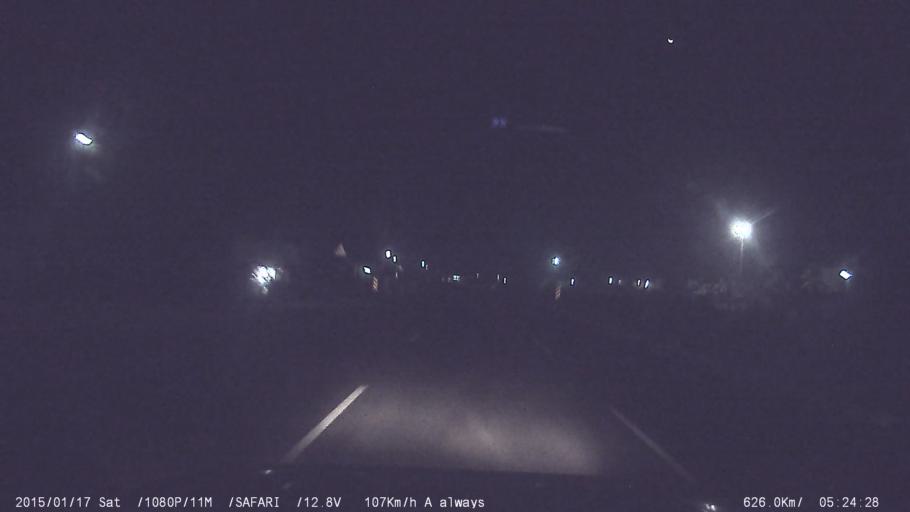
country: IN
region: Tamil Nadu
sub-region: Vellore
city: Katpadi
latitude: 12.9474
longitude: 79.2208
